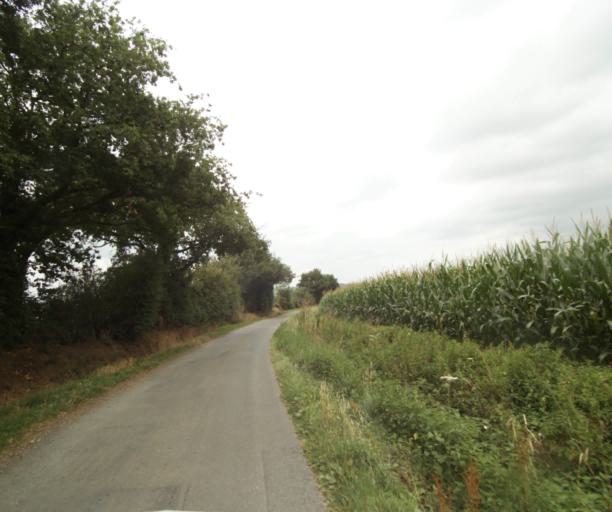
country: FR
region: Pays de la Loire
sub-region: Departement de la Sarthe
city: Juigne-sur-Sarthe
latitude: 47.8495
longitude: -0.2671
